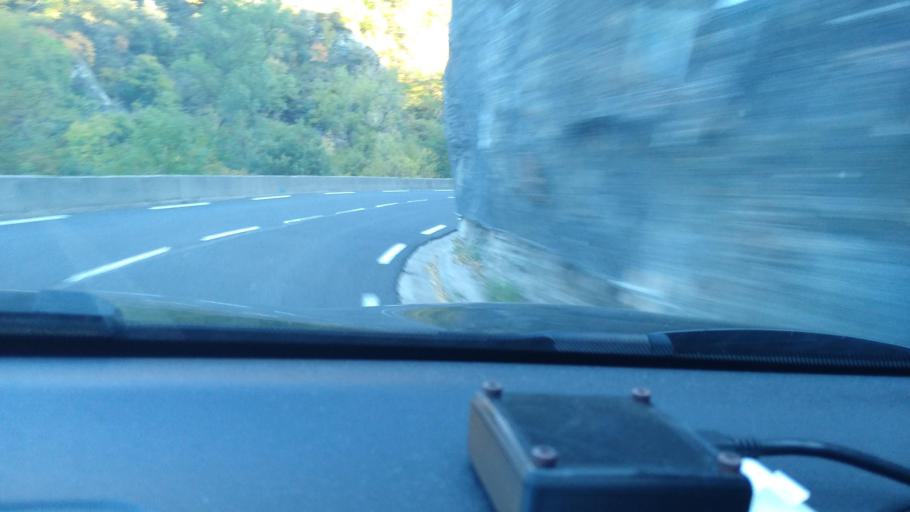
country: FR
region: Languedoc-Roussillon
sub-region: Departement des Pyrenees-Orientales
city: Vernet-les-Bains
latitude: 42.5306
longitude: 2.2479
